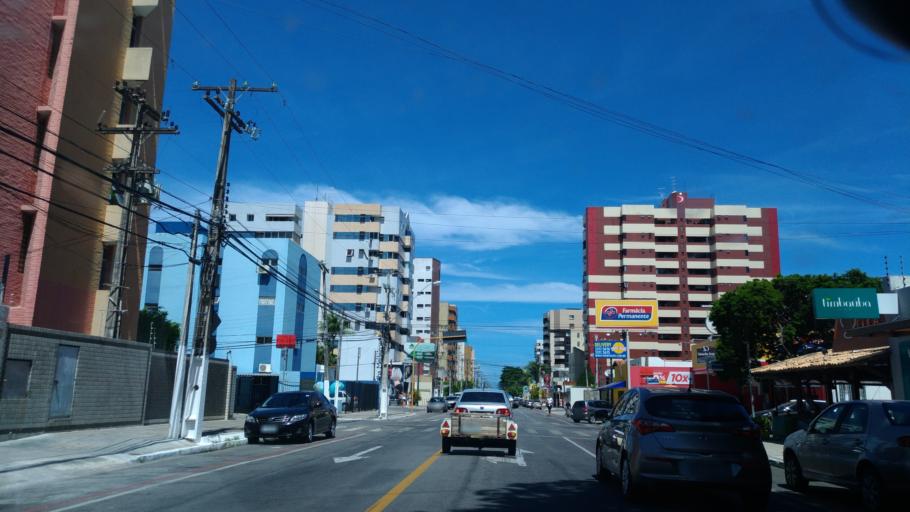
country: BR
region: Alagoas
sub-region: Maceio
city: Maceio
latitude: -9.6567
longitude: -35.7031
